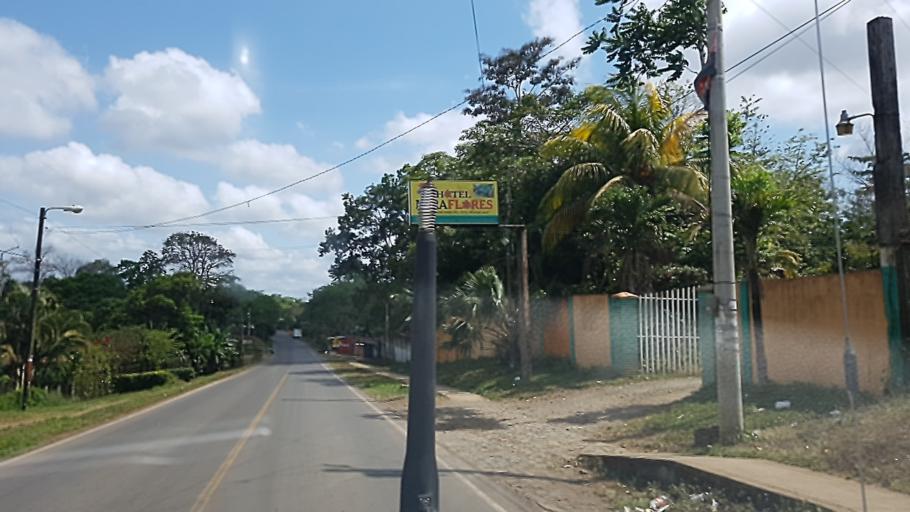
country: NI
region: Atlantico Sur
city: Nueva Guinea
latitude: 11.6931
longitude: -84.4623
